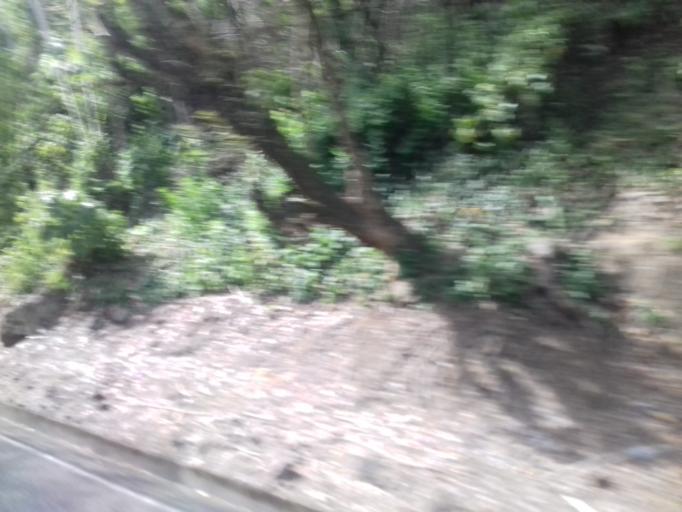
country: CO
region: Antioquia
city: Tarso
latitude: 5.9351
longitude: -75.8511
